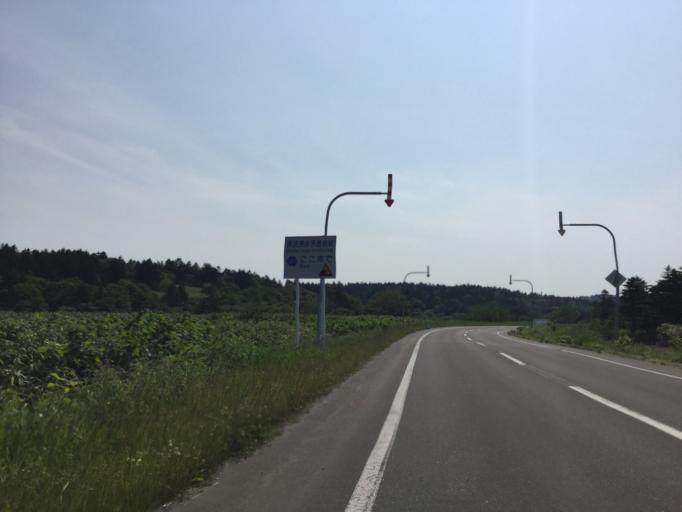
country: JP
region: Hokkaido
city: Makubetsu
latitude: 45.4056
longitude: 142.0410
